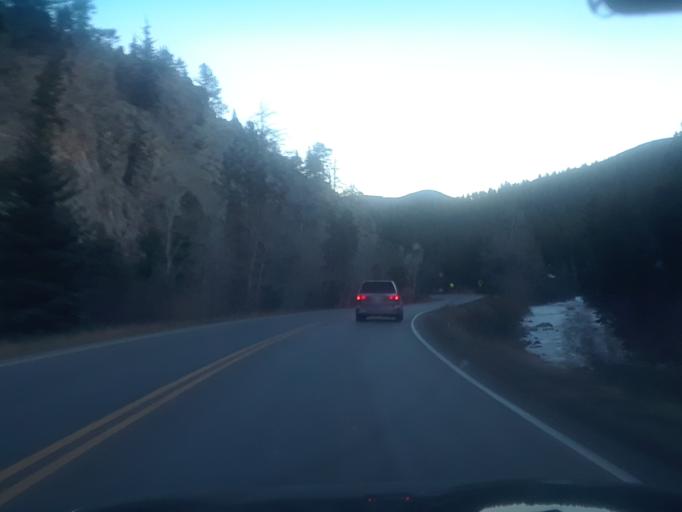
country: US
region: Colorado
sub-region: Jefferson County
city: Evergreen
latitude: 39.4186
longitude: -105.5286
